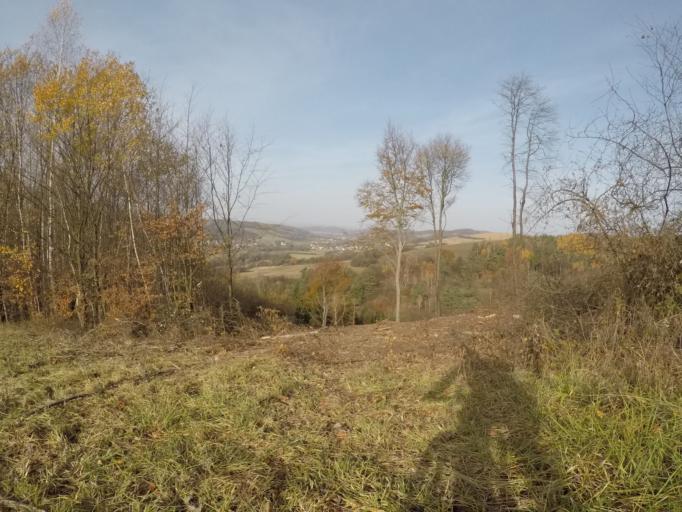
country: SK
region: Presovsky
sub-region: Okres Presov
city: Presov
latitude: 48.9154
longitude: 21.2087
